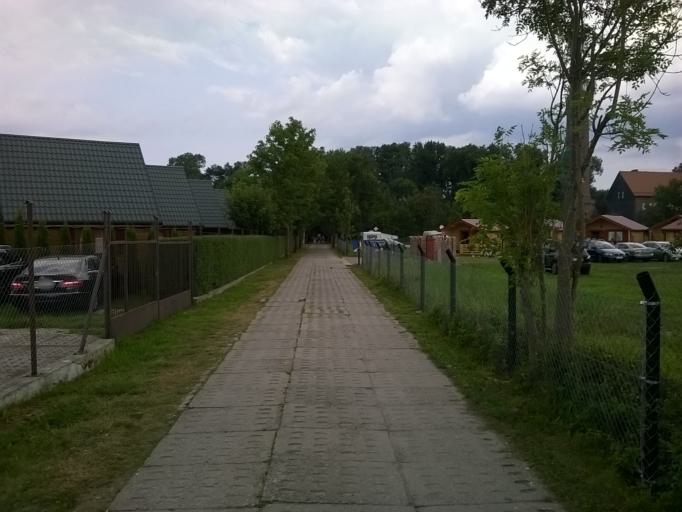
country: PL
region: West Pomeranian Voivodeship
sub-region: Powiat kolobrzeski
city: Ustronie Morskie
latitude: 54.2412
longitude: 15.8719
